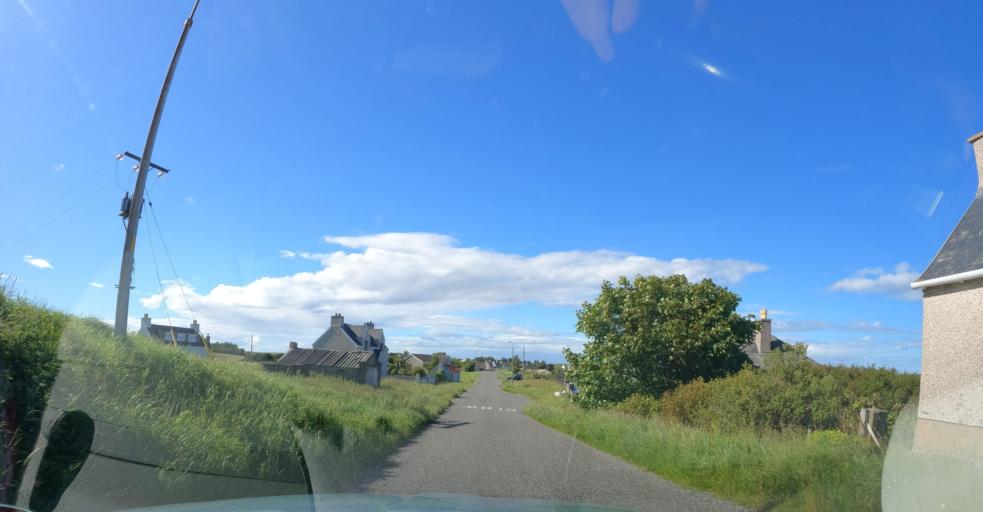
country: GB
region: Scotland
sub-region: Eilean Siar
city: Stornoway
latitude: 58.1966
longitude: -6.2237
